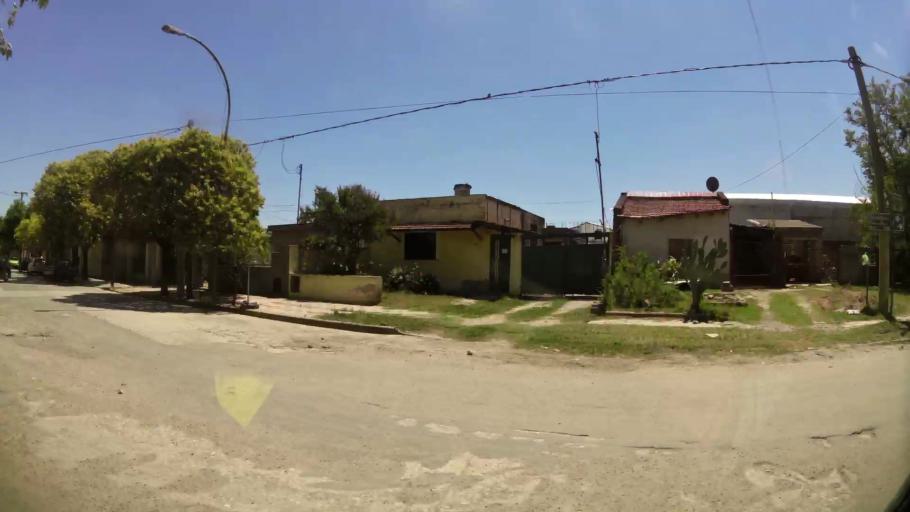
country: AR
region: Cordoba
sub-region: Departamento de Capital
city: Cordoba
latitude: -31.3903
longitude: -64.1479
